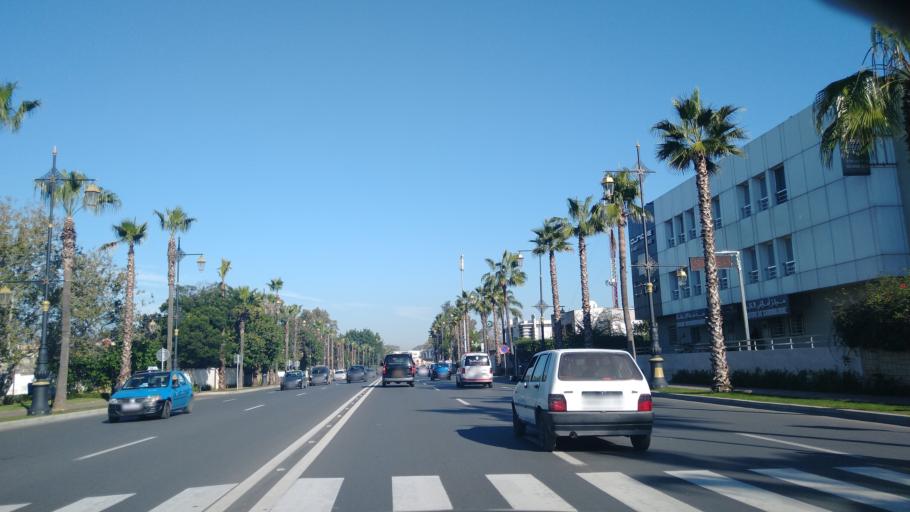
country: MA
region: Rabat-Sale-Zemmour-Zaer
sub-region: Rabat
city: Rabat
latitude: 34.0018
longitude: -6.8273
